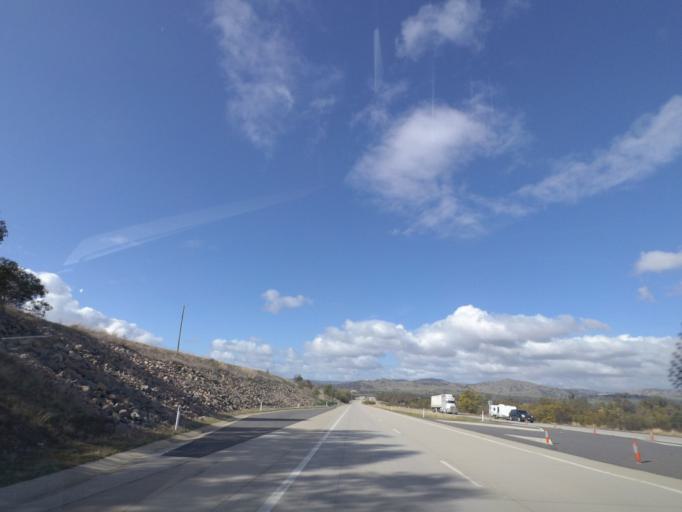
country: AU
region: New South Wales
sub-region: Albury Municipality
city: Lavington
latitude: -35.9154
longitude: 147.1178
